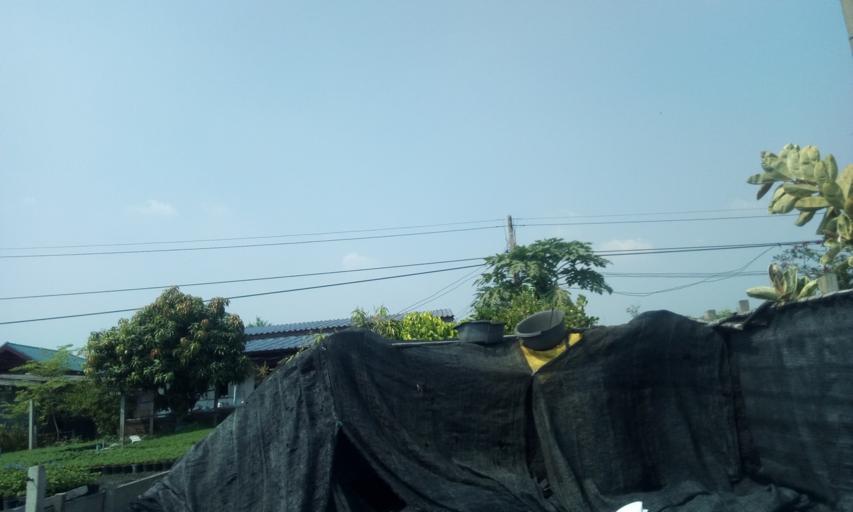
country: TH
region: Nakhon Nayok
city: Ongkharak
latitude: 14.1429
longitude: 100.9764
